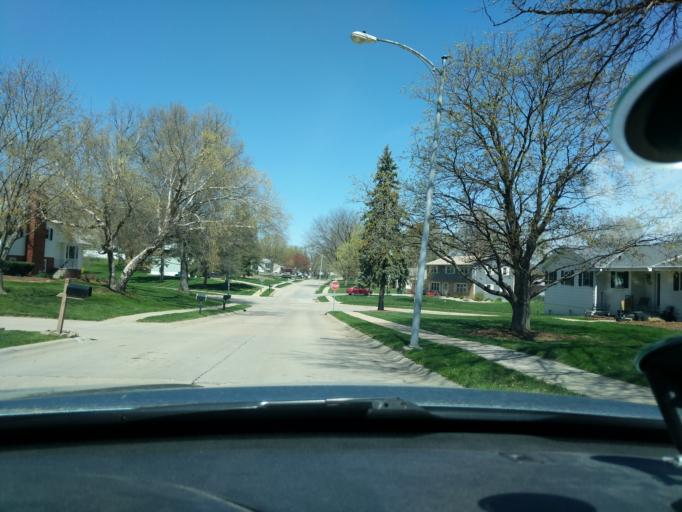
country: US
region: Nebraska
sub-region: Douglas County
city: Ralston
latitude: 41.2279
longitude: -96.0965
